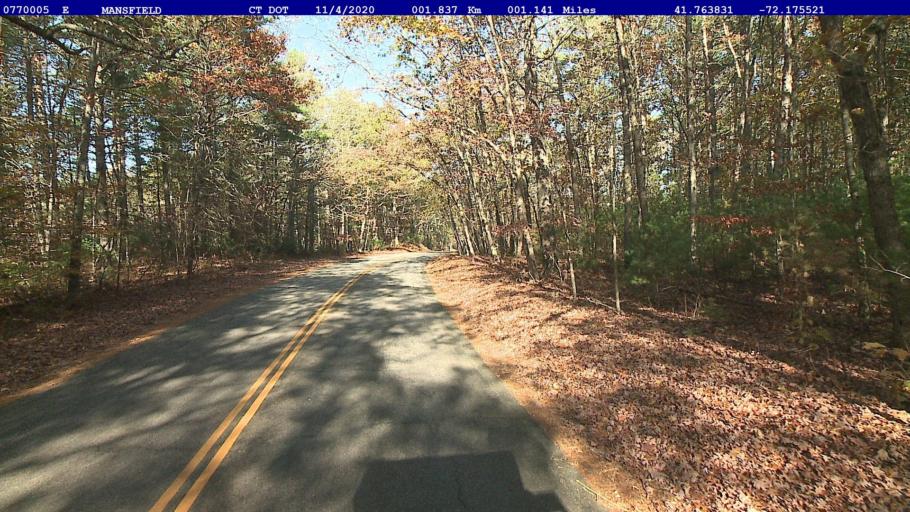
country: US
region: Connecticut
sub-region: Tolland County
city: Mansfield City
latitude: 41.7638
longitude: -72.1755
